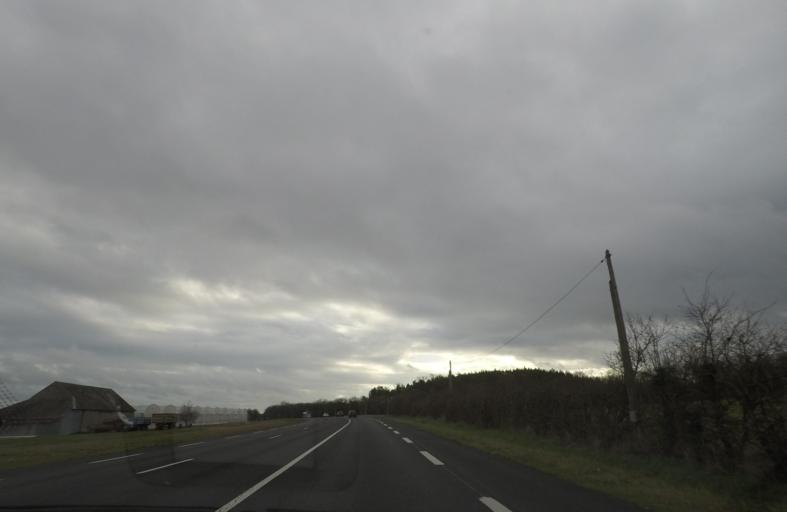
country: FR
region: Centre
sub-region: Departement du Loir-et-Cher
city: Soings-en-Sologne
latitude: 47.4415
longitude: 1.5460
